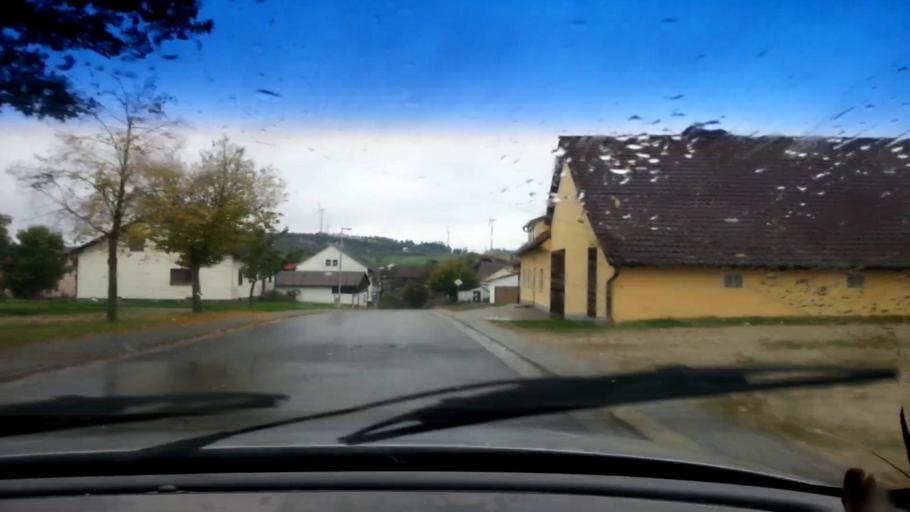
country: DE
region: Bavaria
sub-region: Upper Franconia
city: Poxdorf
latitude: 49.9364
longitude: 11.1241
